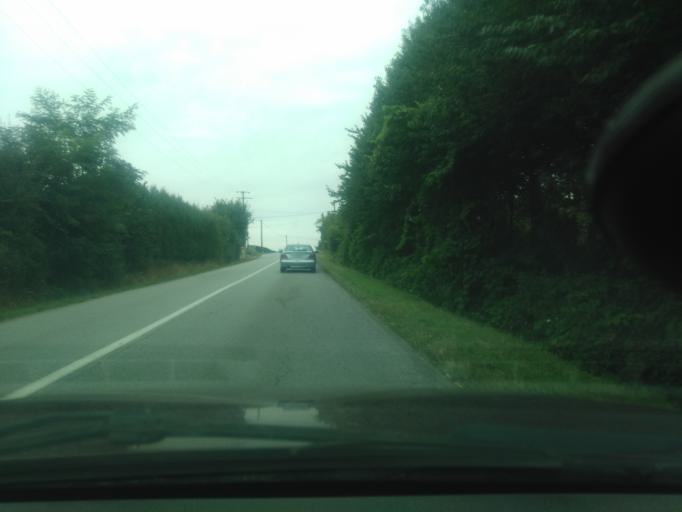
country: FR
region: Poitou-Charentes
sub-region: Departement des Deux-Sevres
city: Saint-Aubin-le-Cloud
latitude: 46.6238
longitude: -0.3424
